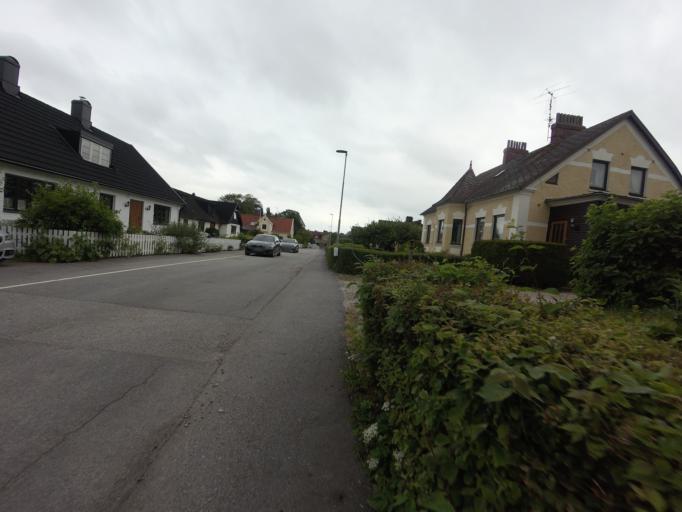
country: SE
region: Skane
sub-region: Staffanstorps Kommun
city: Hjaerup
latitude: 55.6490
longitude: 13.1157
